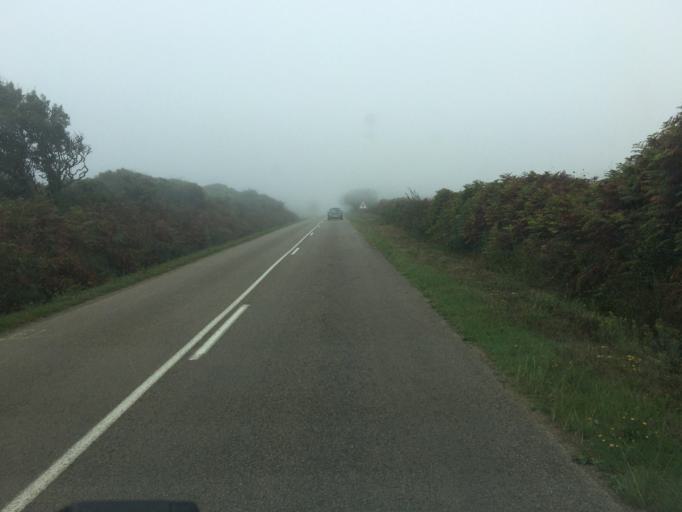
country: FR
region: Brittany
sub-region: Departement du Finistere
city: Plogoff
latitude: 48.0566
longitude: -4.6741
